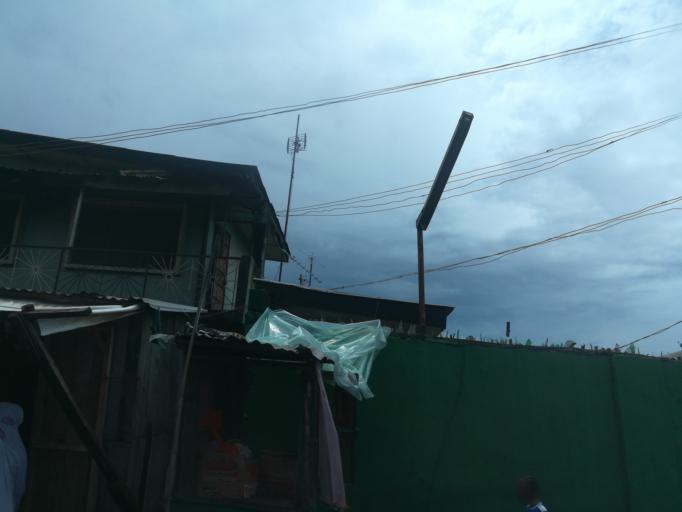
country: NG
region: Lagos
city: Agege
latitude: 6.6163
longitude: 3.3324
